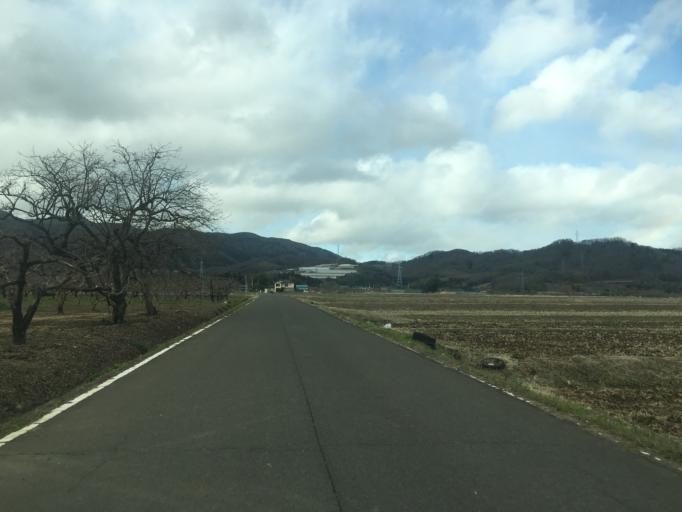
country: JP
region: Fukushima
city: Yanagawamachi-saiwaicho
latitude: 37.8831
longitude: 140.5820
